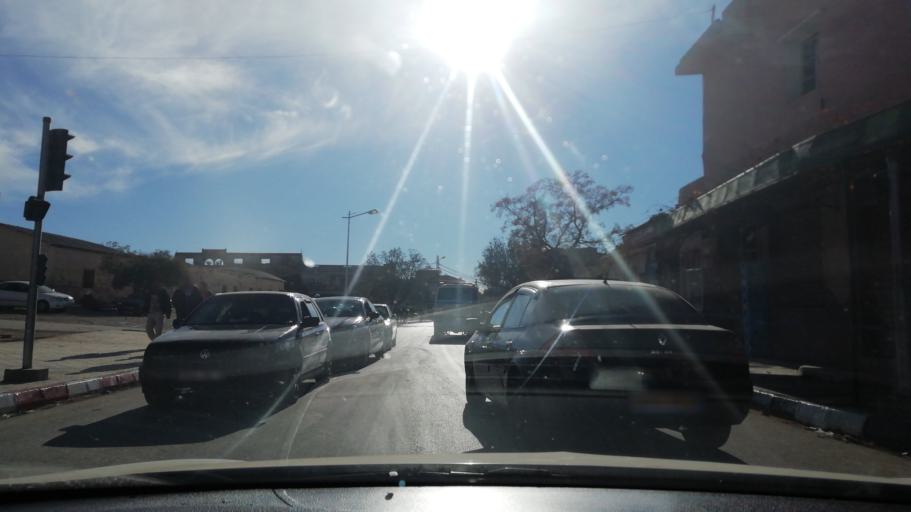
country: DZ
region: Tlemcen
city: Sebdou
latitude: 34.6473
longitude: -1.3220
